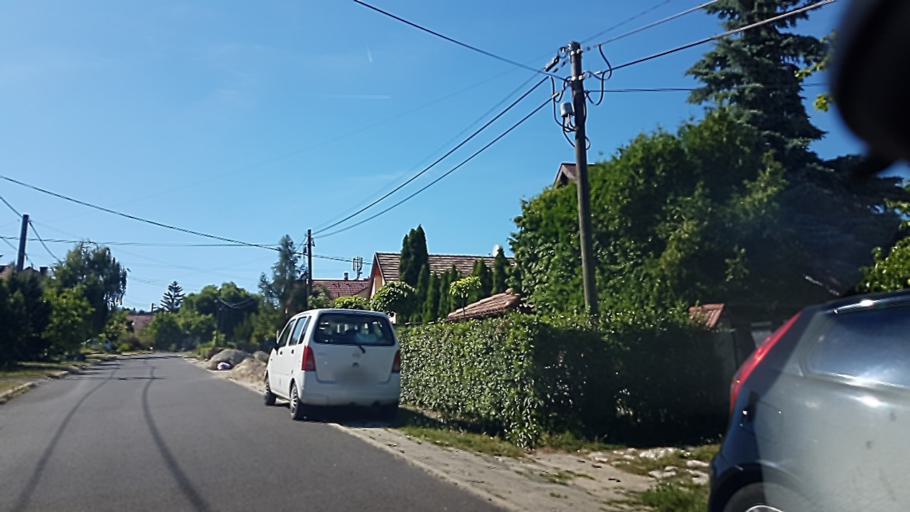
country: HU
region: Pest
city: Pilisszentivan
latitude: 47.6071
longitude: 18.8915
